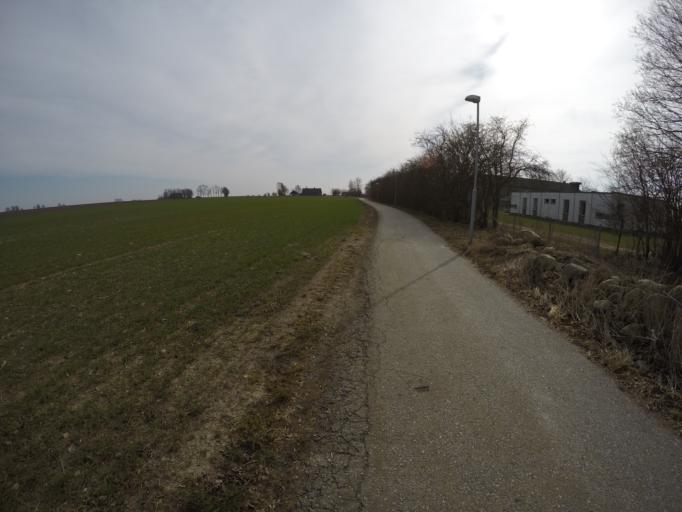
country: SE
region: Skane
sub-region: Ystads Kommun
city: Kopingebro
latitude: 55.4310
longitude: 14.1146
